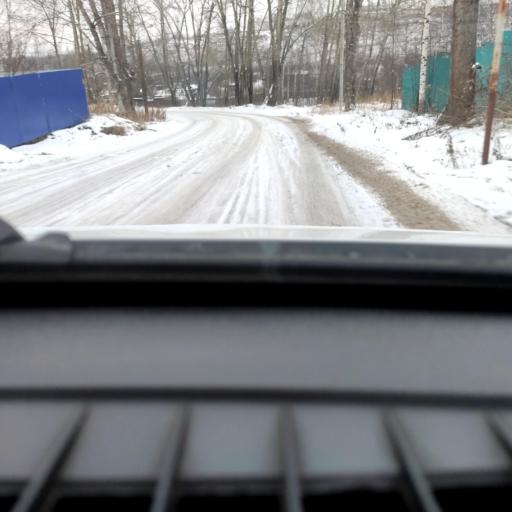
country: RU
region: Perm
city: Perm
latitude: 58.1036
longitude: 56.3660
